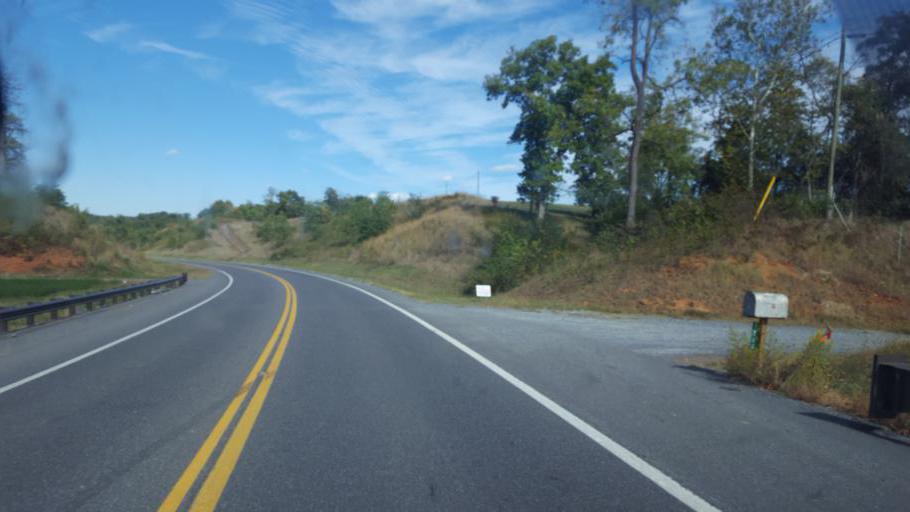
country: US
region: Virginia
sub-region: Page County
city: Luray
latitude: 38.7763
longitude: -78.3751
